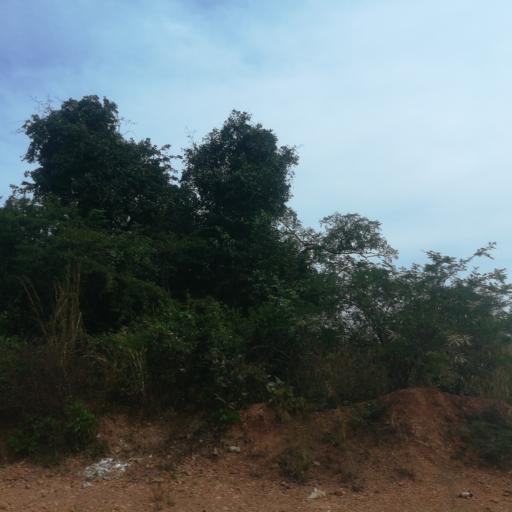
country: NG
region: Plateau
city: Jos
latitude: 9.8898
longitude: 8.8396
